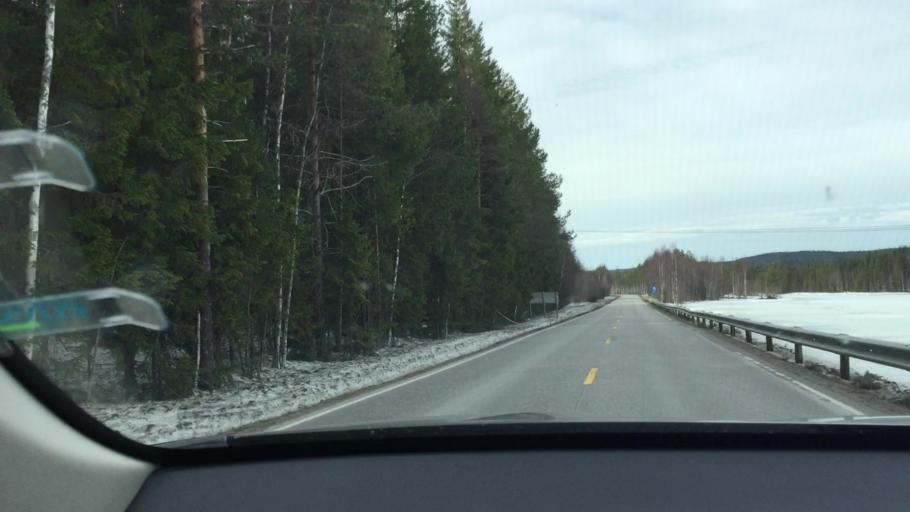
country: NO
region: Hedmark
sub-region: Trysil
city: Innbygda
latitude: 61.0687
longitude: 12.5793
